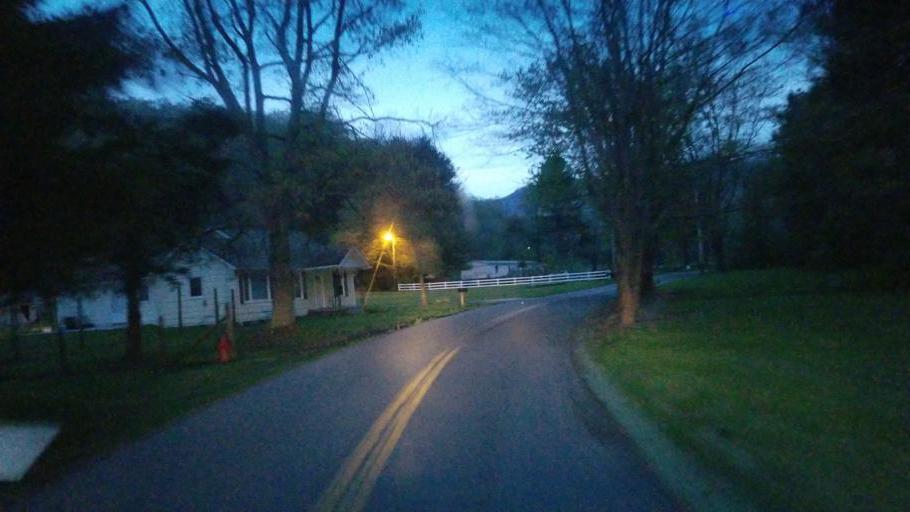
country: US
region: Virginia
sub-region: Smyth County
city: Atkins
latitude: 36.8393
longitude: -81.4565
